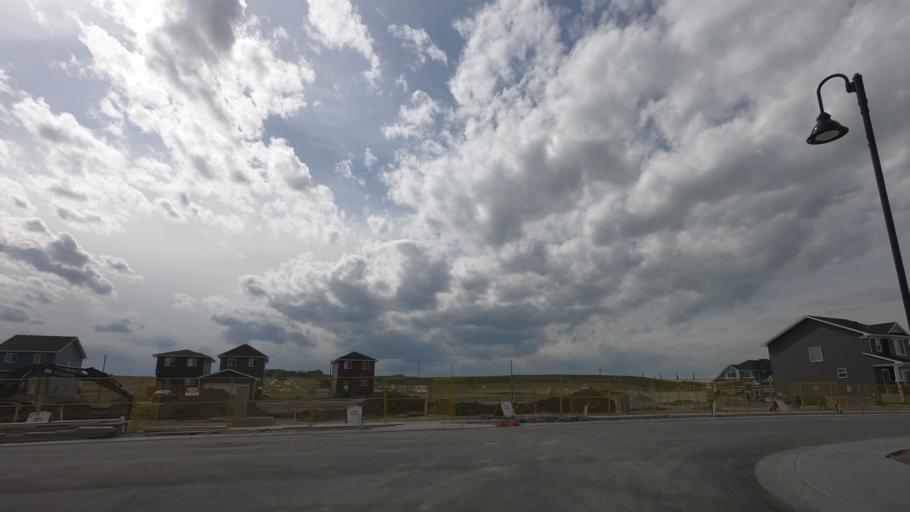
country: CA
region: Alberta
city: Airdrie
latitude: 51.2799
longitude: -114.0422
